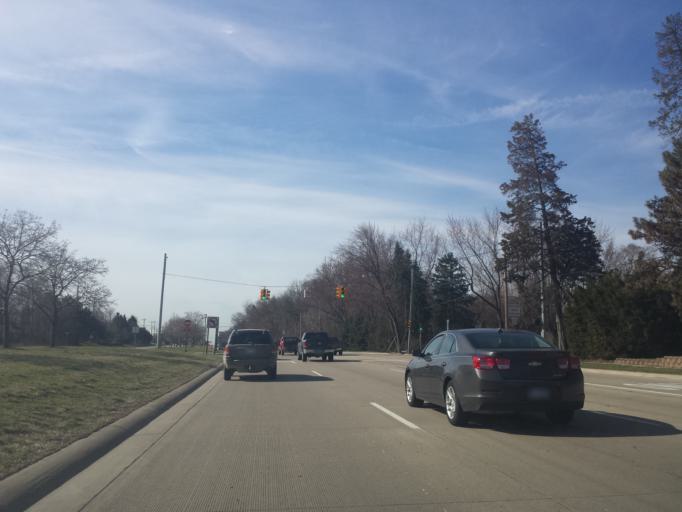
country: US
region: Michigan
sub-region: Oakland County
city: Franklin
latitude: 42.5592
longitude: -83.2855
